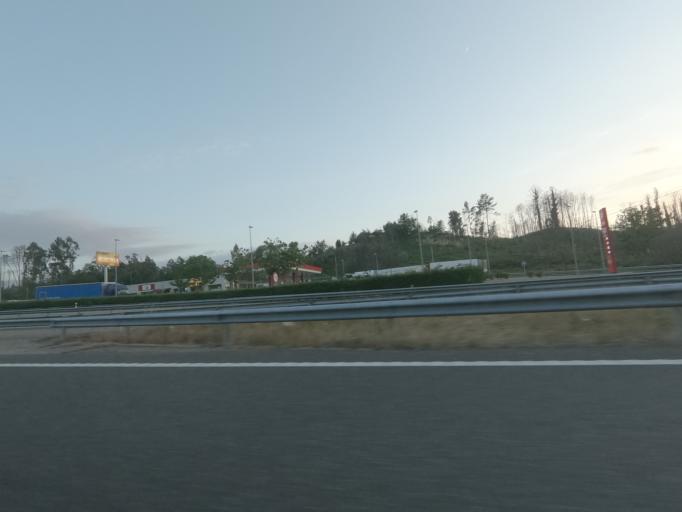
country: ES
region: Galicia
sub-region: Provincia de Pontevedra
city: Ponteareas
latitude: 42.1464
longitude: -8.4759
